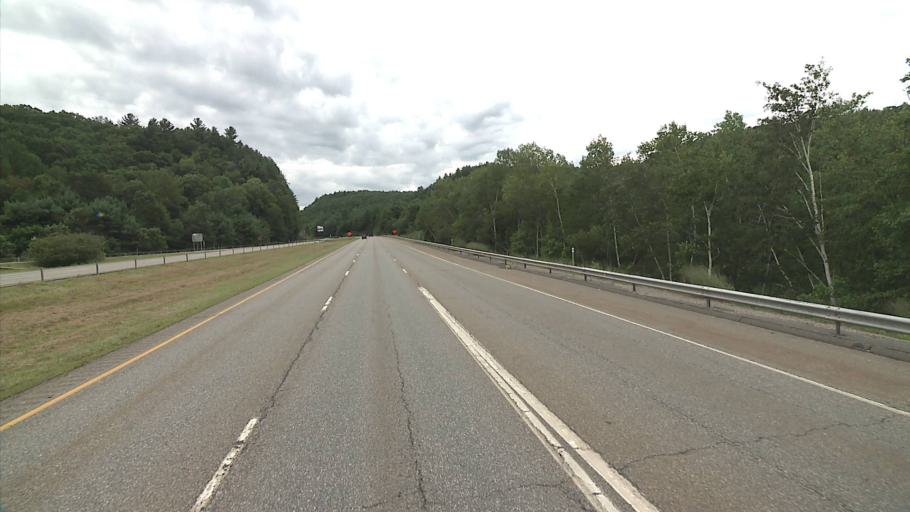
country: US
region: Connecticut
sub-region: Litchfield County
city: Northwest Harwinton
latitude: 41.7602
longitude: -73.1156
